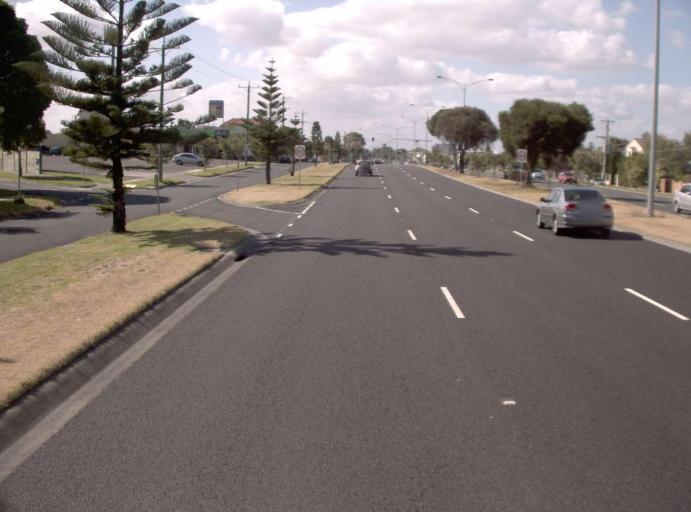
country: AU
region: Victoria
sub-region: Kingston
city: Mentone
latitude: -37.9717
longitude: 145.0628
